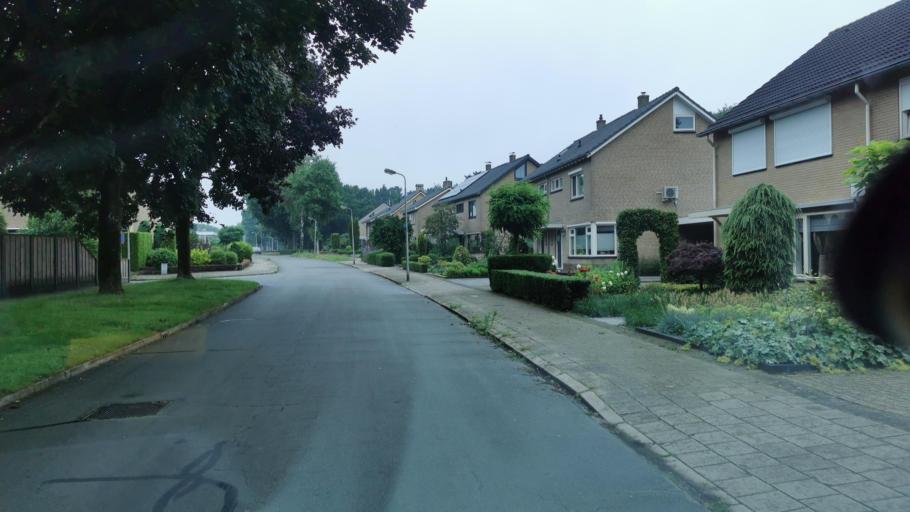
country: NL
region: Overijssel
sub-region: Gemeente Losser
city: Losser
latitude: 52.2541
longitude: 7.0078
